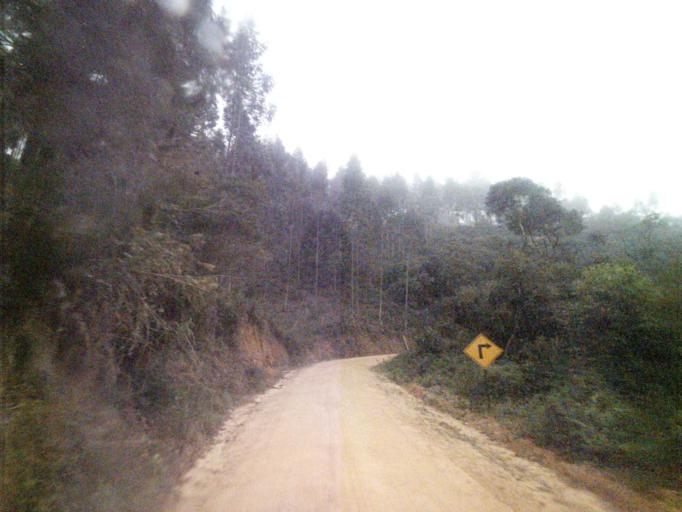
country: BR
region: Santa Catarina
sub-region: Anitapolis
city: Anitapolis
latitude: -27.8224
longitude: -49.1366
